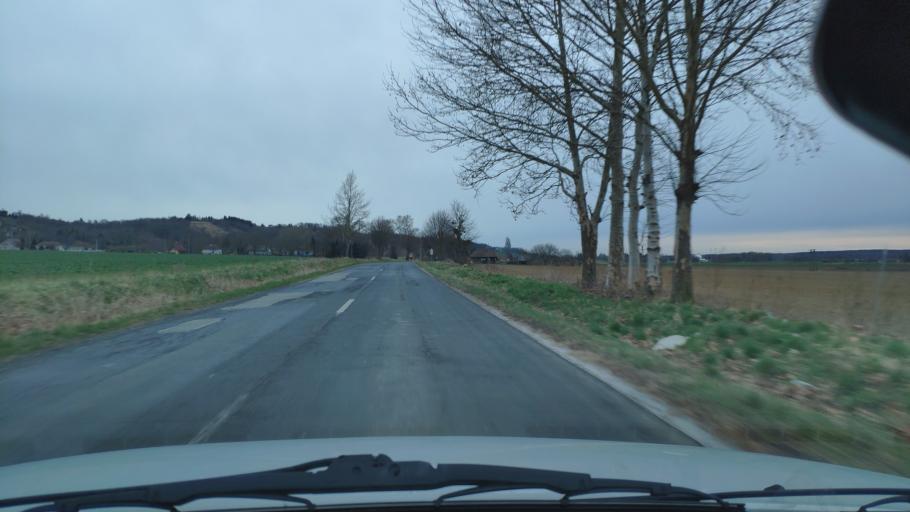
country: HU
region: Zala
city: Nagykanizsa
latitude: 46.5586
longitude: 16.9896
